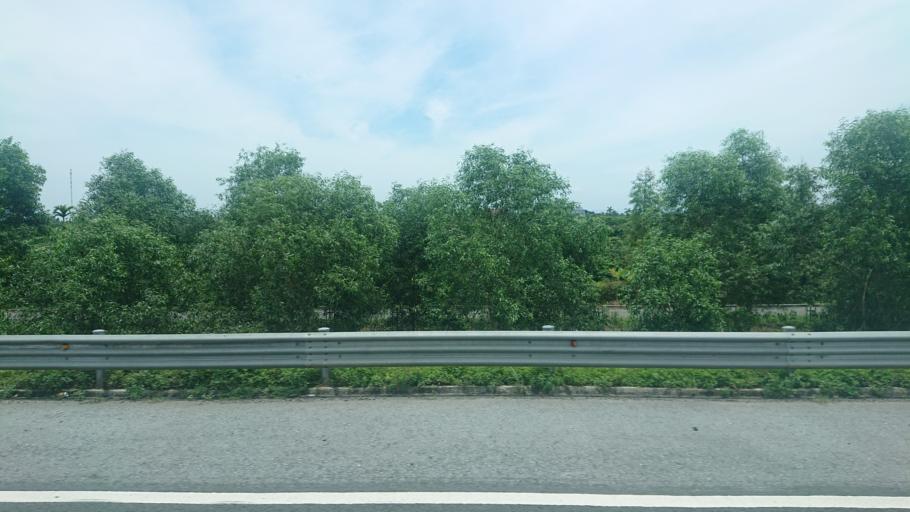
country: VN
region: Hai Duong
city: Tu Ky
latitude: 20.8248
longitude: 106.4658
